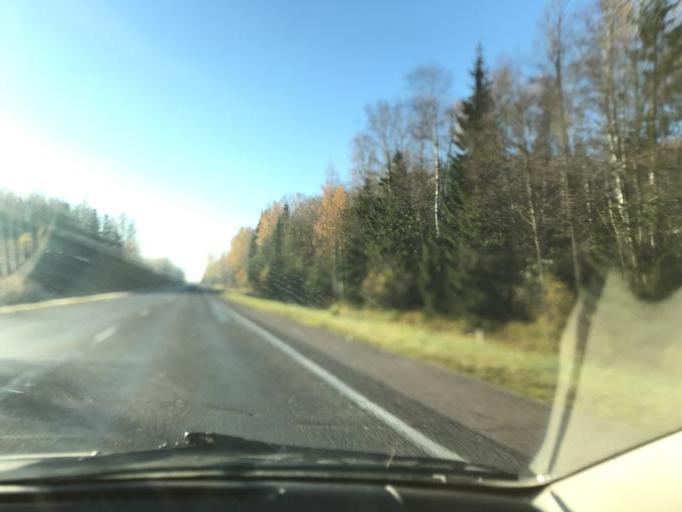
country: BY
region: Vitebsk
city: Vitebsk
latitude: 54.9424
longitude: 30.3649
